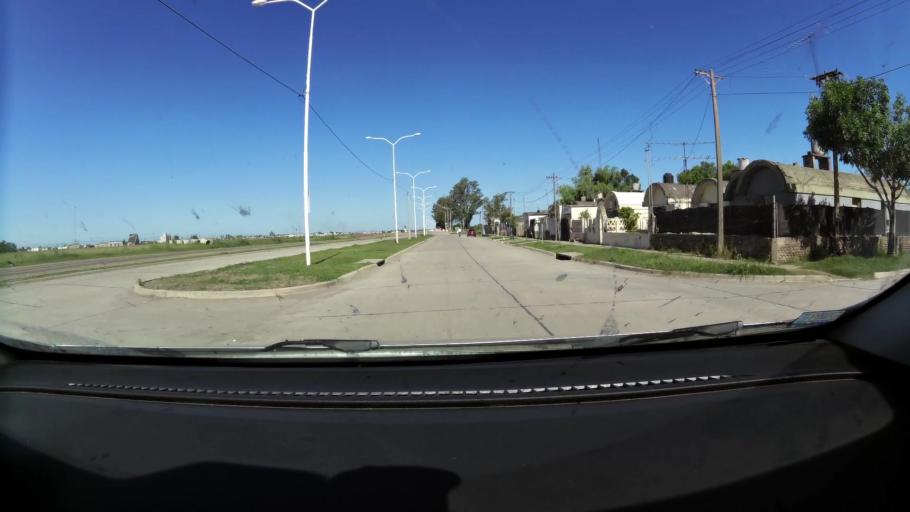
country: AR
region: Santa Fe
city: Rafaela
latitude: -31.2349
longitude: -61.4831
